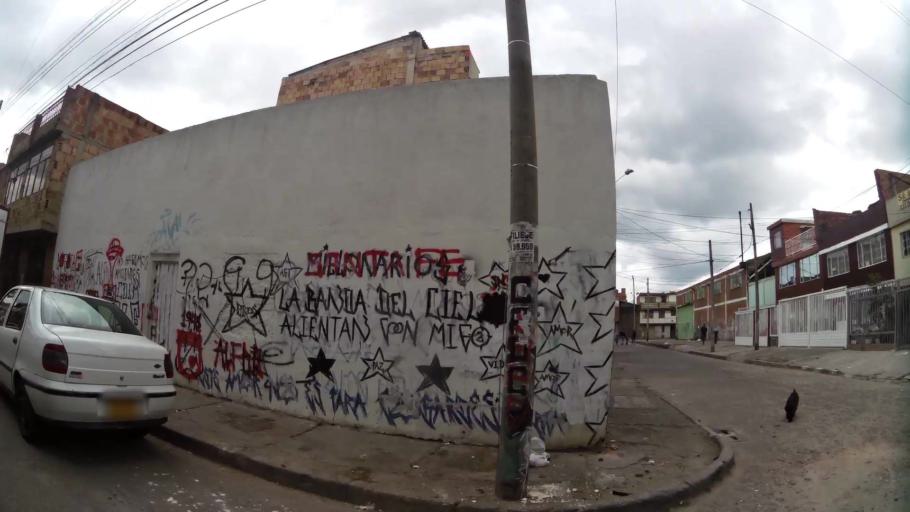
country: CO
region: Bogota D.C.
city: Bogota
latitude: 4.6060
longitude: -74.1331
